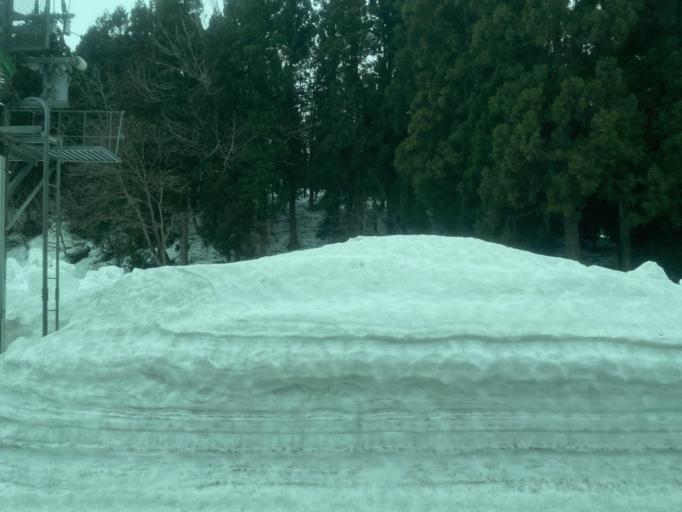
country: JP
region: Niigata
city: Shiozawa
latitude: 36.9252
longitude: 138.8285
